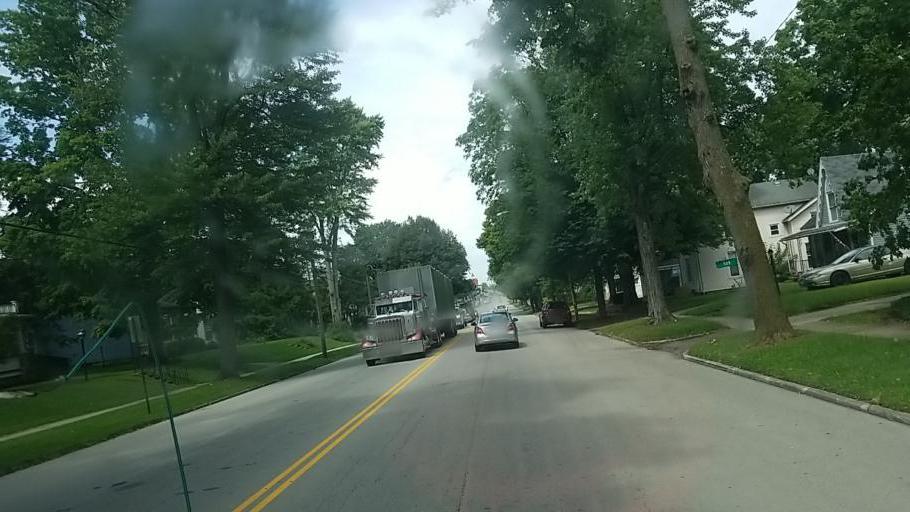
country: US
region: Ohio
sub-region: Champaign County
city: Urbana
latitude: 40.1021
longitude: -83.7531
